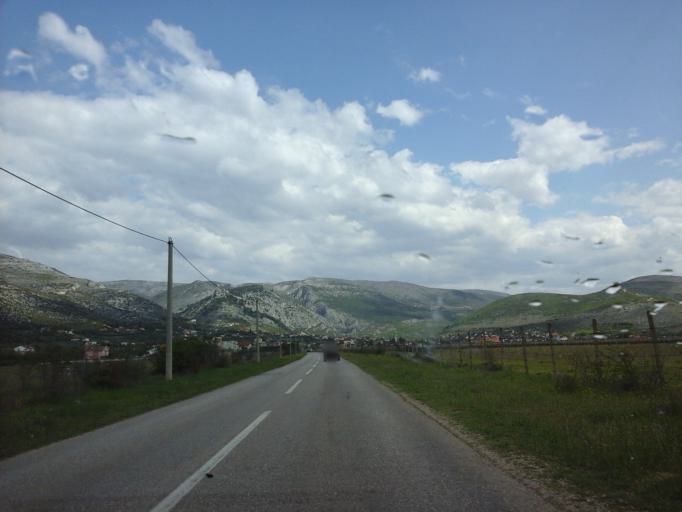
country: BA
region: Federation of Bosnia and Herzegovina
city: Blagaj
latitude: 43.2676
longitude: 17.8679
